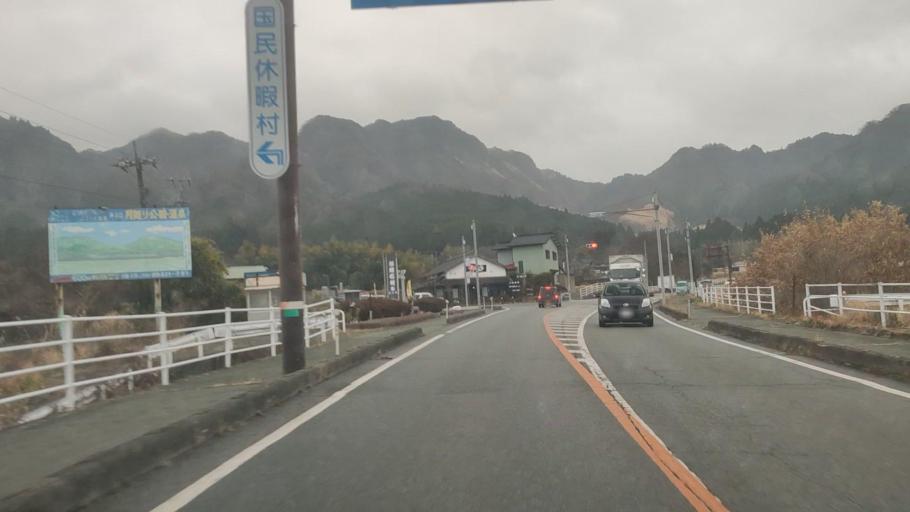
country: JP
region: Kumamoto
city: Aso
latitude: 32.8274
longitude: 131.1314
